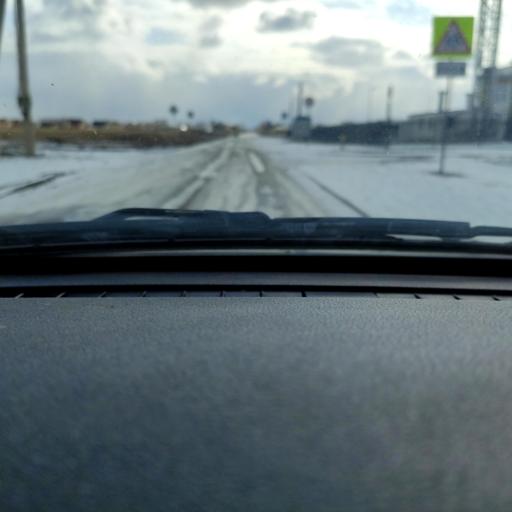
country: RU
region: Voronezj
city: Novaya Usman'
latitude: 51.6615
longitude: 39.4536
